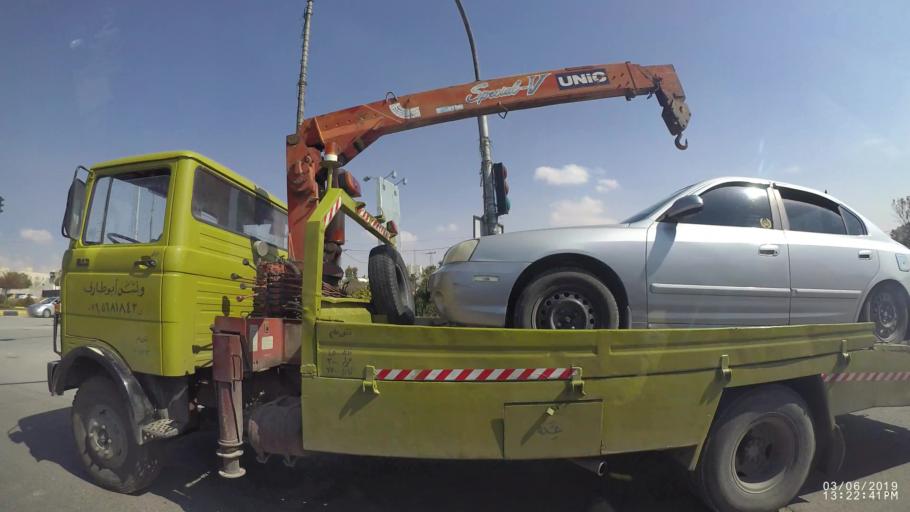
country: JO
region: Zarqa
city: Zarqa
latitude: 32.0512
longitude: 36.0932
